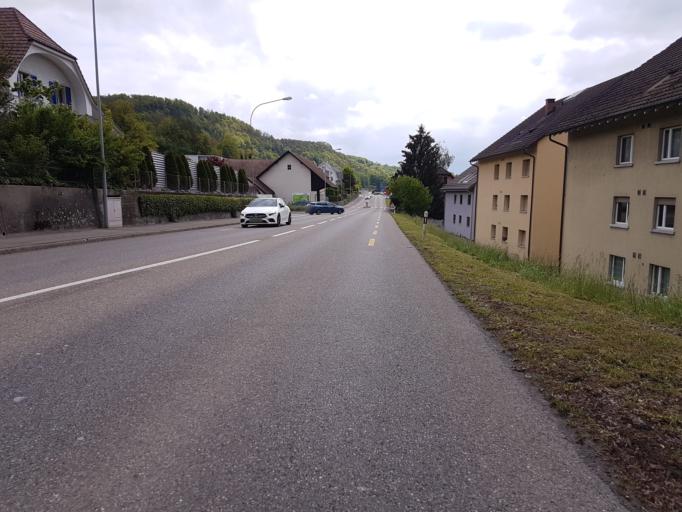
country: CH
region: Aargau
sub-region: Bezirk Brugg
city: Schinznach Bad
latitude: 47.4527
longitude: 8.1680
